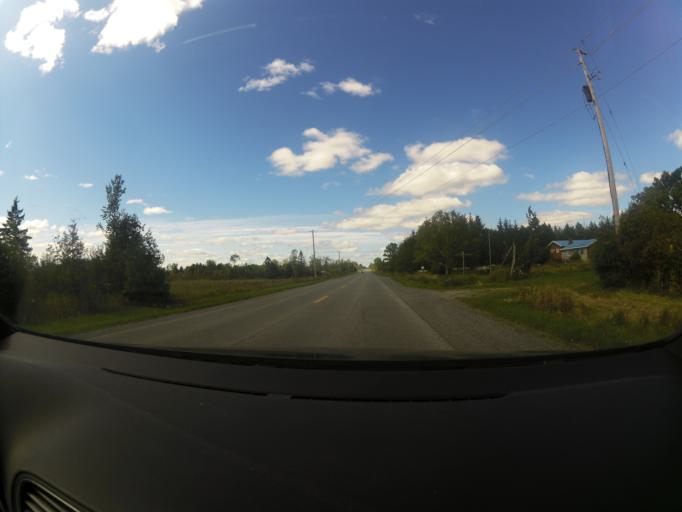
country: CA
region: Ontario
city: Carleton Place
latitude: 45.2287
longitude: -76.1685
